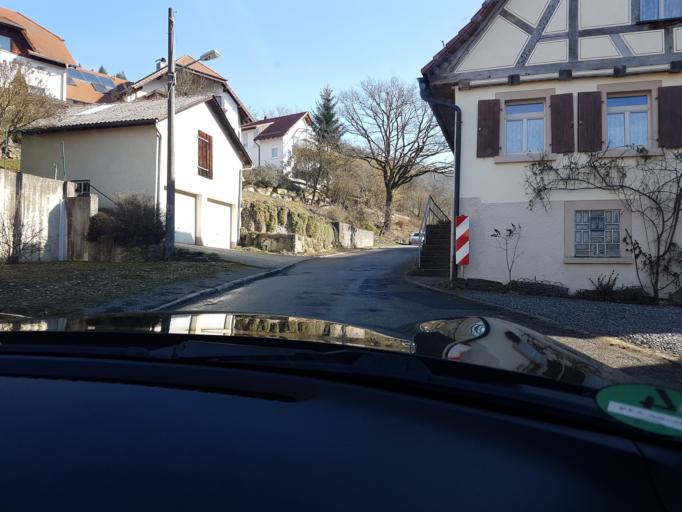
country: DE
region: Baden-Wuerttemberg
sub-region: Regierungsbezirk Stuttgart
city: Mulfingen
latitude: 49.2983
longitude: 9.8299
